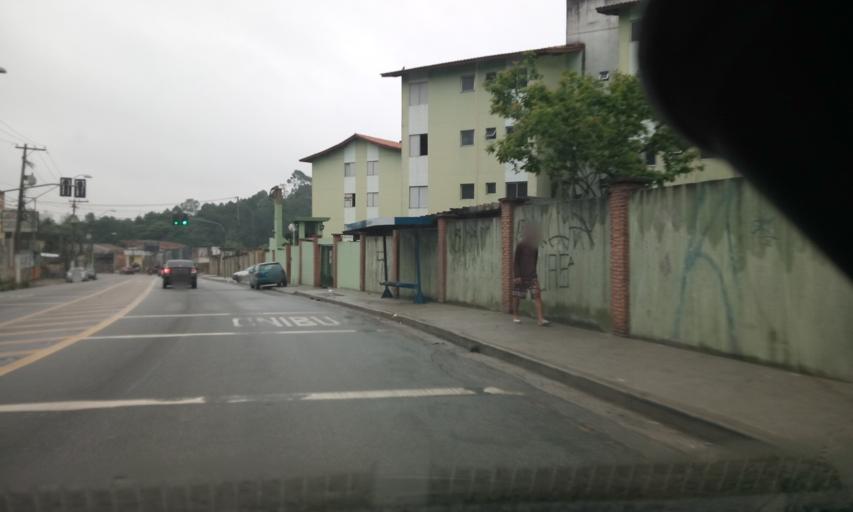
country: BR
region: Sao Paulo
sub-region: Santo Andre
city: Santo Andre
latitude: -23.7055
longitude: -46.5199
